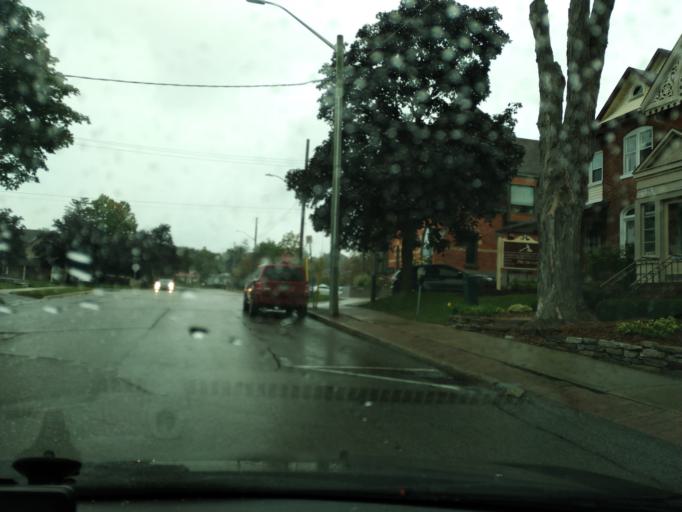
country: CA
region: Ontario
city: Barrie
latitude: 44.3911
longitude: -79.6901
